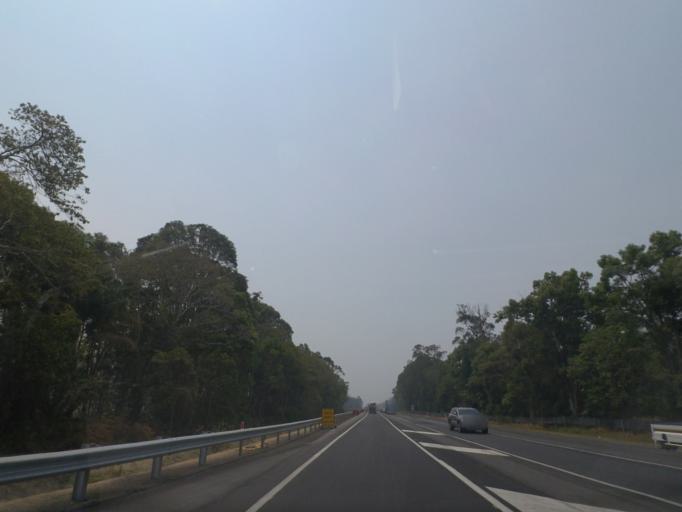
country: AU
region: New South Wales
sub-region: Ballina
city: Ballina
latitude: -28.9189
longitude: 153.4767
